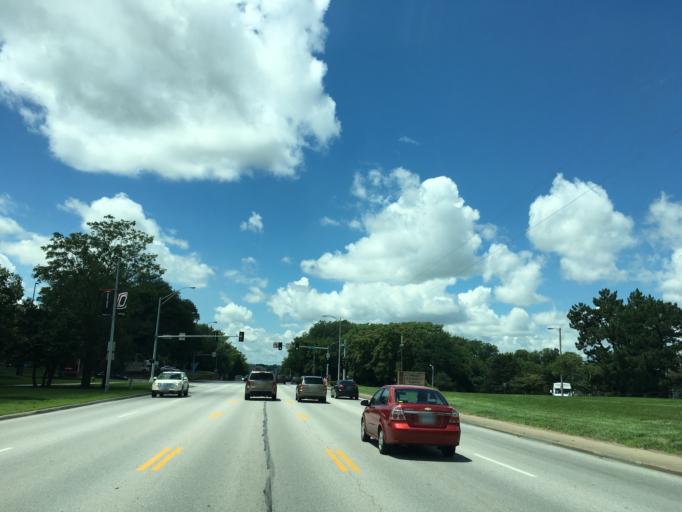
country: US
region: Nebraska
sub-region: Douglas County
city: Ralston
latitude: 41.2596
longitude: -96.0136
